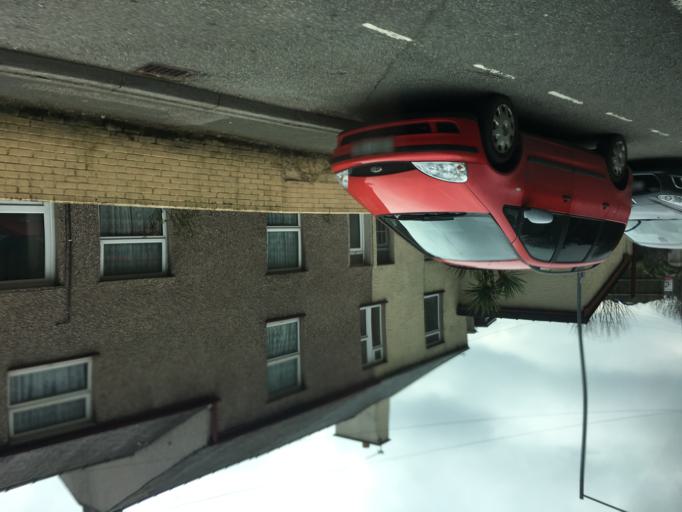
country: GB
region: Wales
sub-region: Gwynedd
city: Y Felinheli
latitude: 53.1837
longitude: -4.2095
